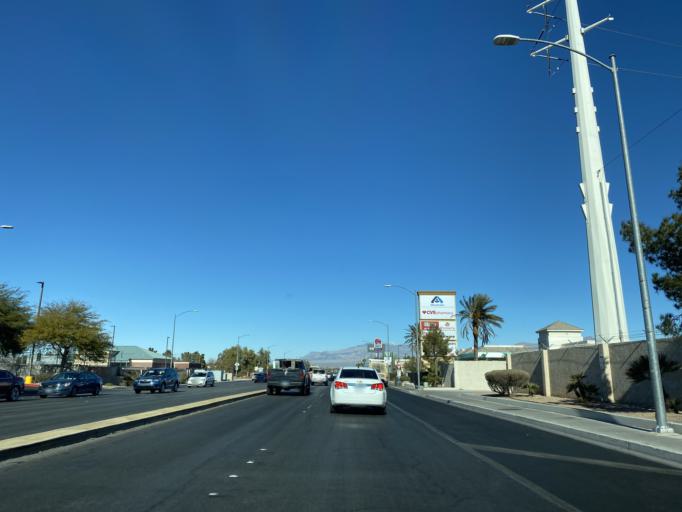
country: US
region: Nevada
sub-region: Clark County
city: Summerlin South
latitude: 36.2189
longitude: -115.2787
